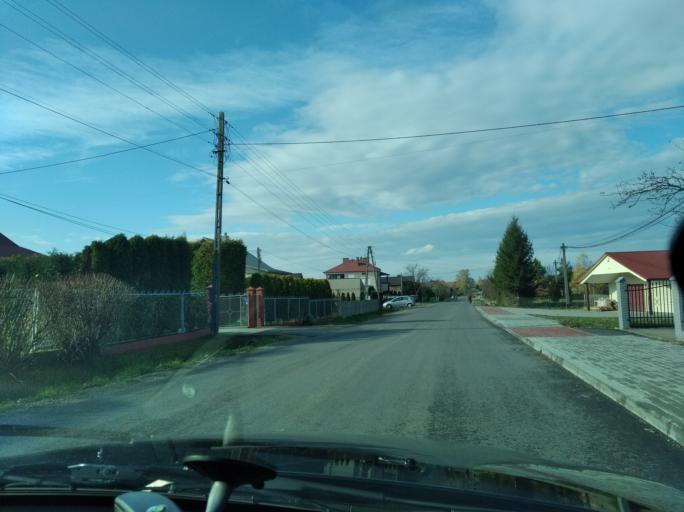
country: PL
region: Subcarpathian Voivodeship
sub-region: Powiat ropczycko-sedziszowski
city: Iwierzyce
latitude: 50.0755
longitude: 21.7490
